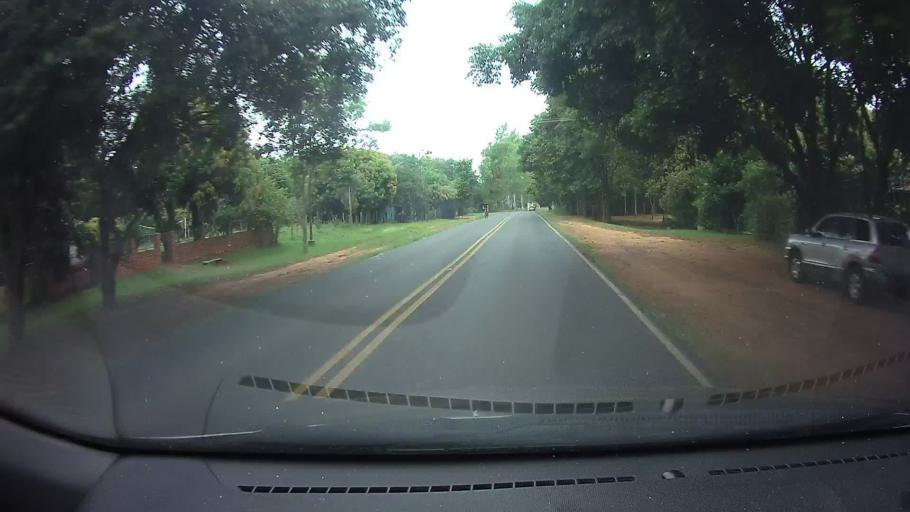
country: PY
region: Central
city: Nueva Italia
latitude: -25.5473
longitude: -57.4994
